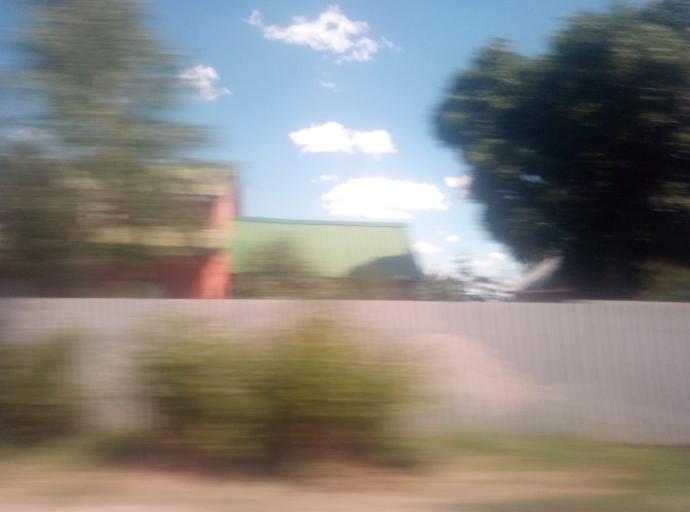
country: RU
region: Tula
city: Kireyevsk
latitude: 53.9699
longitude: 37.9317
